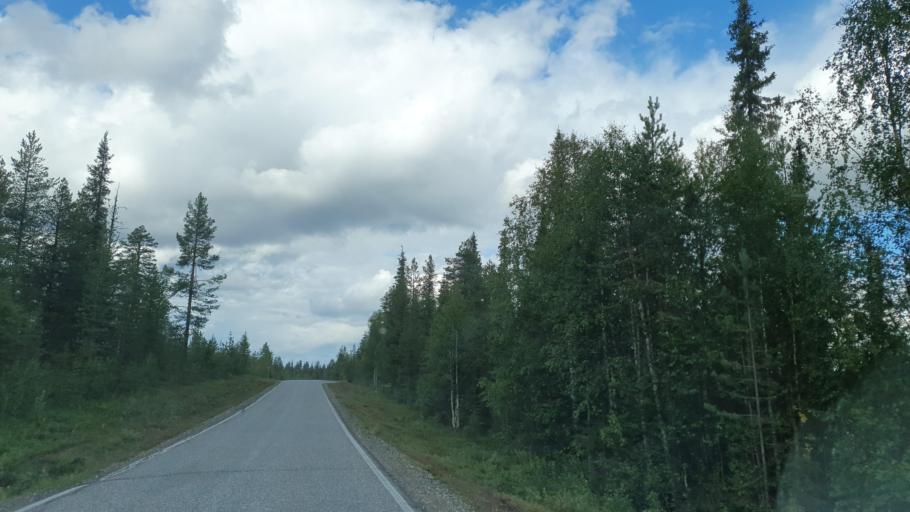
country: FI
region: Lapland
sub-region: Tunturi-Lappi
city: Muonio
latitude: 67.7701
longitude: 24.0944
